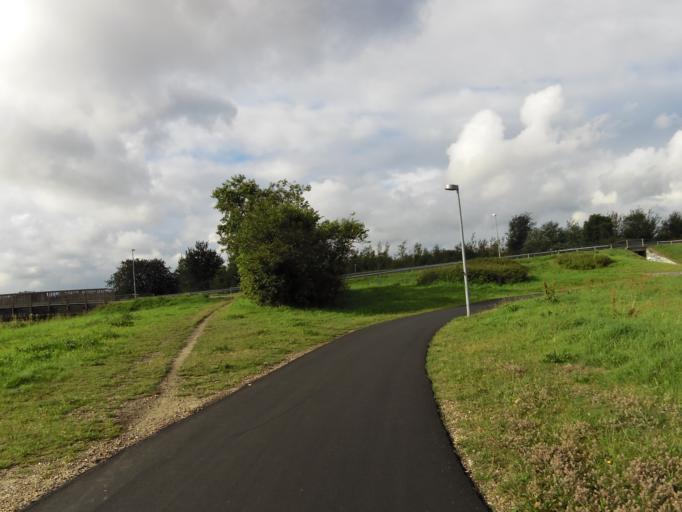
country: DK
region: South Denmark
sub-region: Esbjerg Kommune
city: Ribe
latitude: 55.3365
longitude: 8.7809
